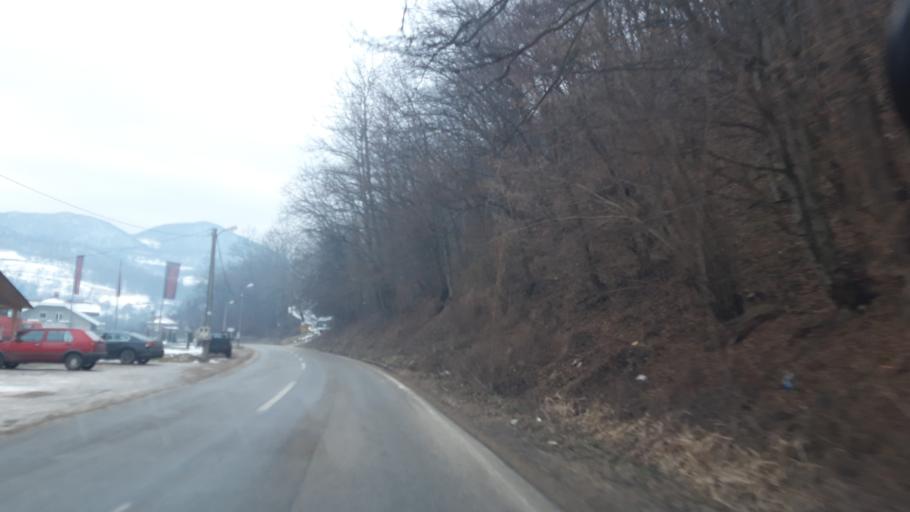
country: BA
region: Republika Srpska
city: Milici
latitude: 44.1662
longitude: 19.0696
